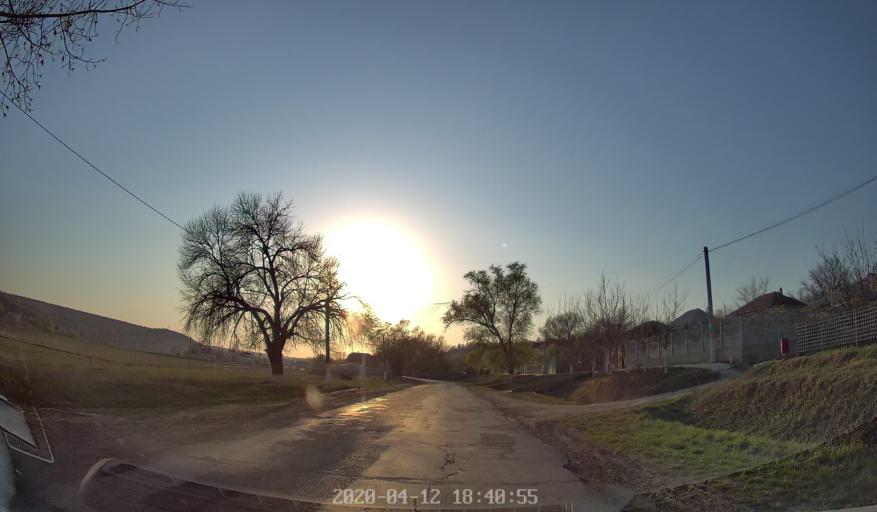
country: MD
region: Chisinau
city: Ciorescu
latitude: 47.1355
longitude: 28.9600
